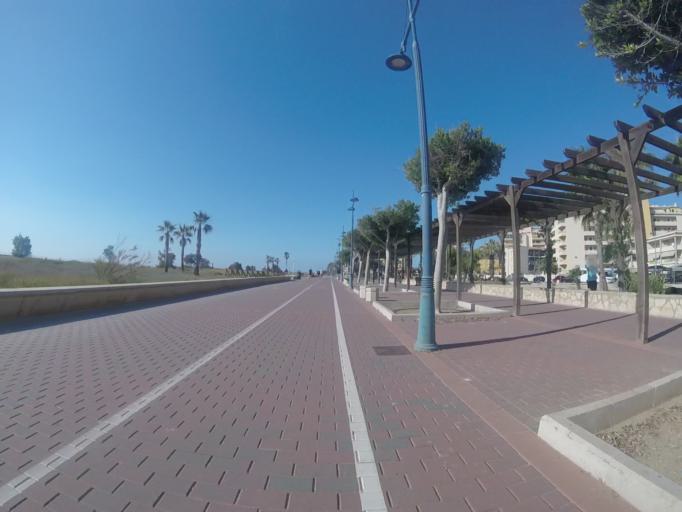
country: ES
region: Valencia
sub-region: Provincia de Castello
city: Peniscola
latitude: 40.3827
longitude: 0.4089
